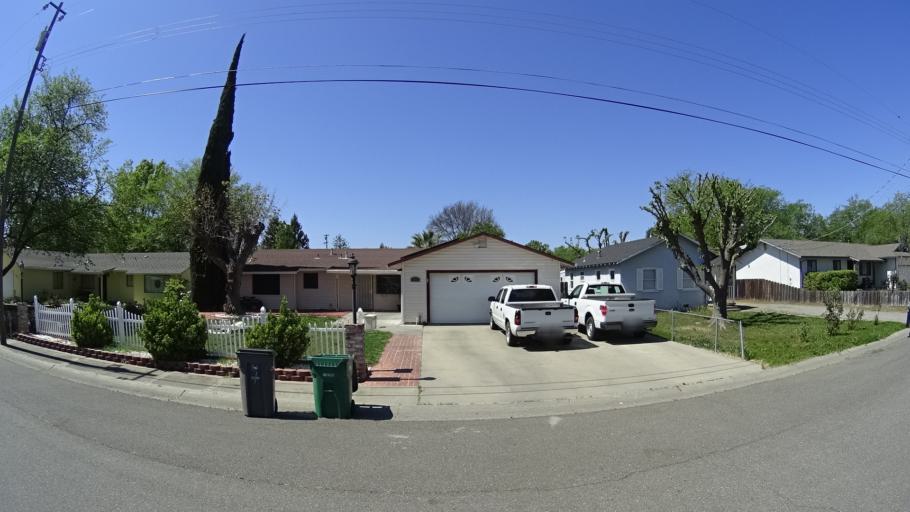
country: US
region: California
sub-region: Glenn County
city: Willows
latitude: 39.5282
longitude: -122.1969
